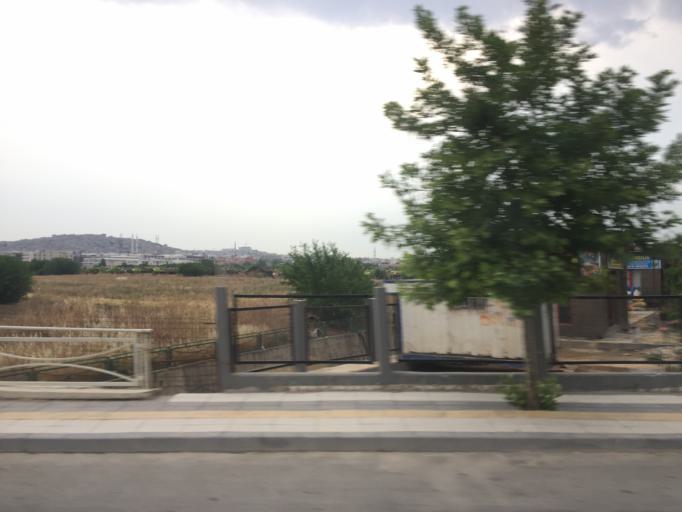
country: TR
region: Gaziantep
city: Gaziantep
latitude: 37.0595
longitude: 37.4157
